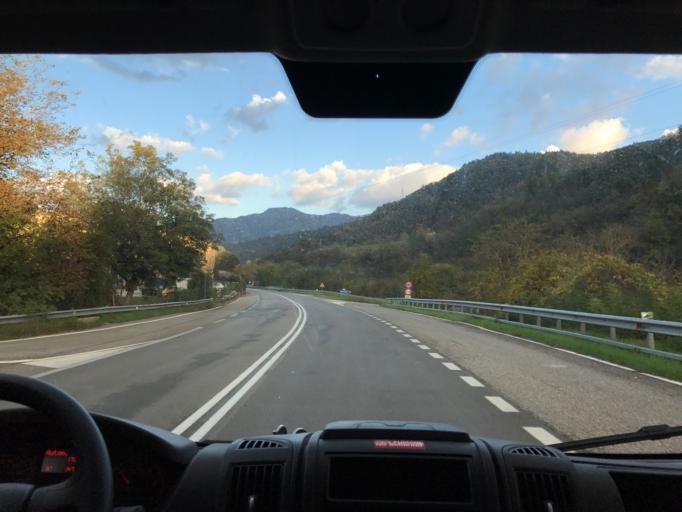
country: IT
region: The Marches
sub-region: Provincia di Ascoli Piceno
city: Marsia
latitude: 42.8020
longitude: 13.4722
